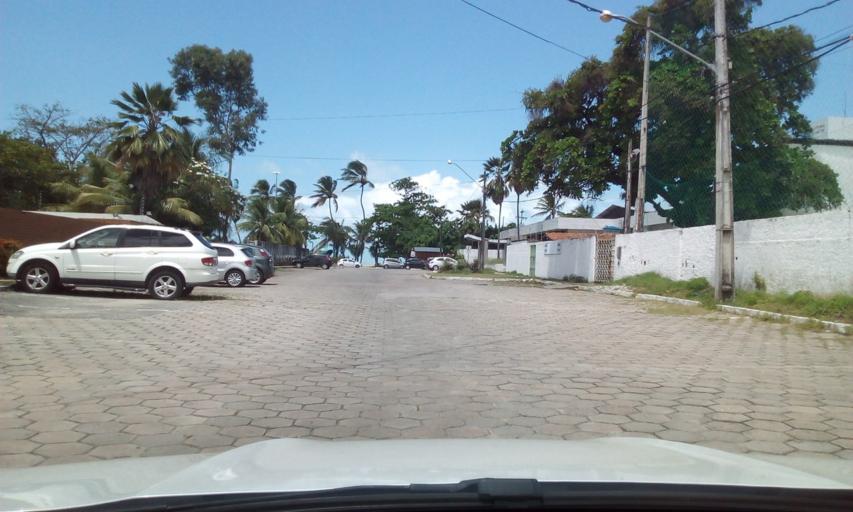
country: BR
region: Paraiba
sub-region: Joao Pessoa
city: Joao Pessoa
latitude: -7.1289
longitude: -34.8240
